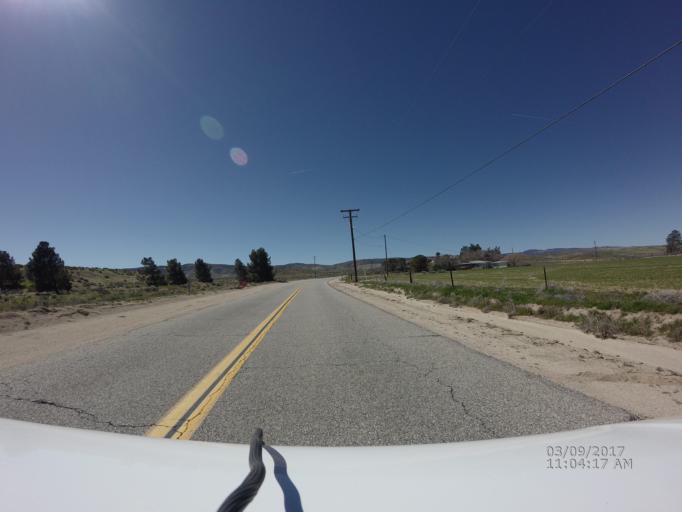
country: US
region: California
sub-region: Los Angeles County
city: Green Valley
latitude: 34.7097
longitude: -118.3550
